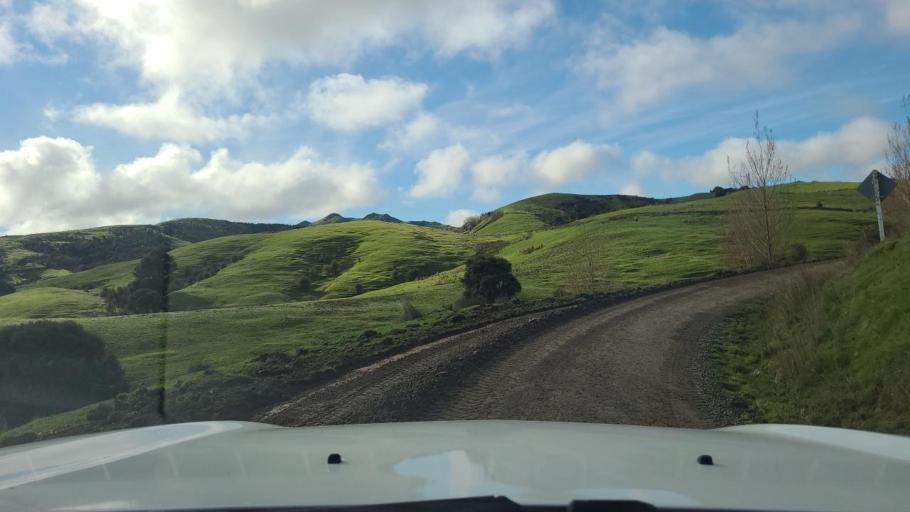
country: NZ
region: Wellington
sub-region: South Wairarapa District
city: Waipawa
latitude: -41.2410
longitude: 175.6875
